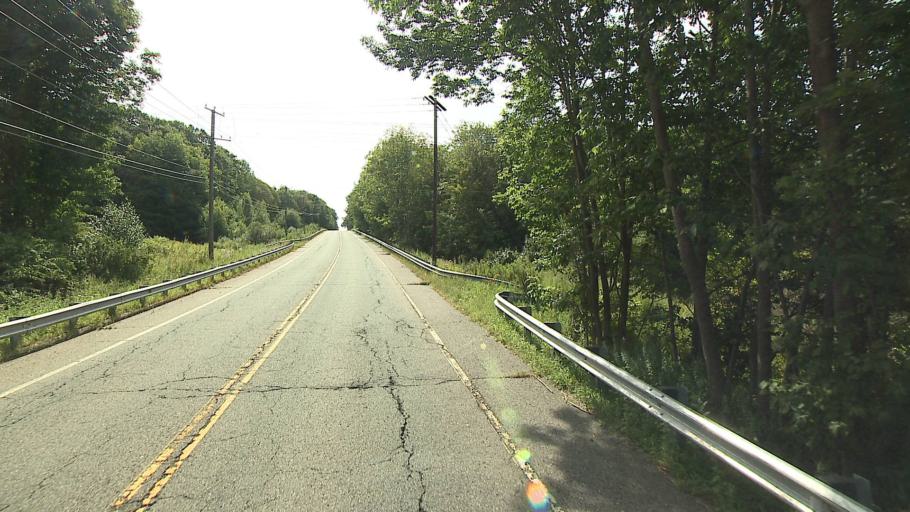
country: US
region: Connecticut
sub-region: Litchfield County
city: Litchfield
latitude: 41.7311
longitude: -73.1566
